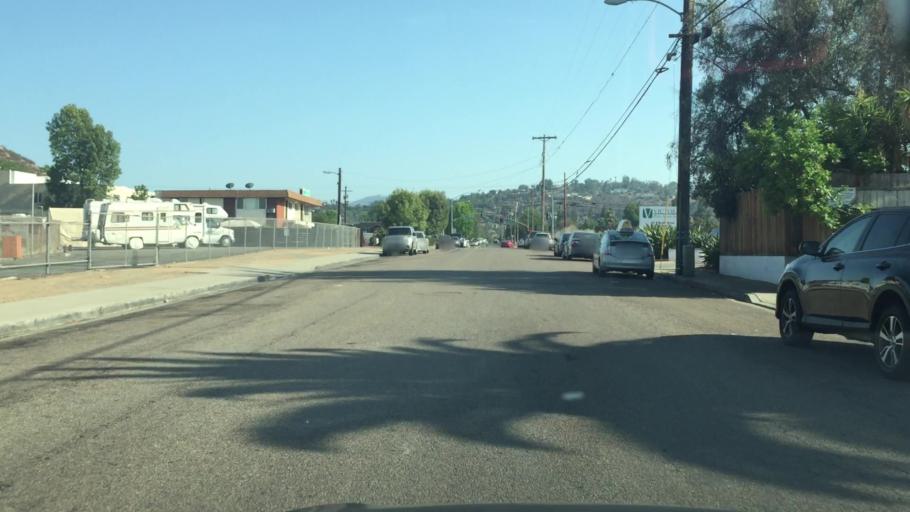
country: US
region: California
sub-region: San Diego County
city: El Cajon
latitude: 32.7894
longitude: -116.9482
